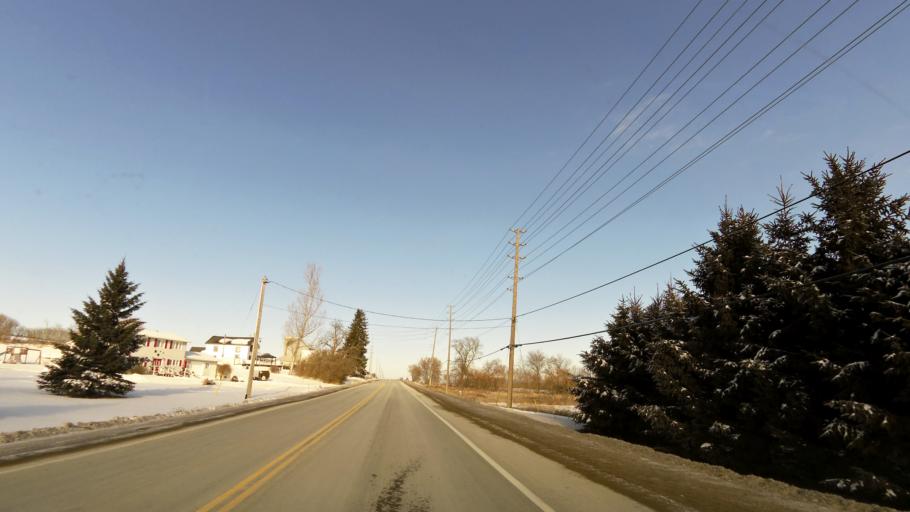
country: CA
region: Ontario
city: Quinte West
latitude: 44.1641
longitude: -77.8018
